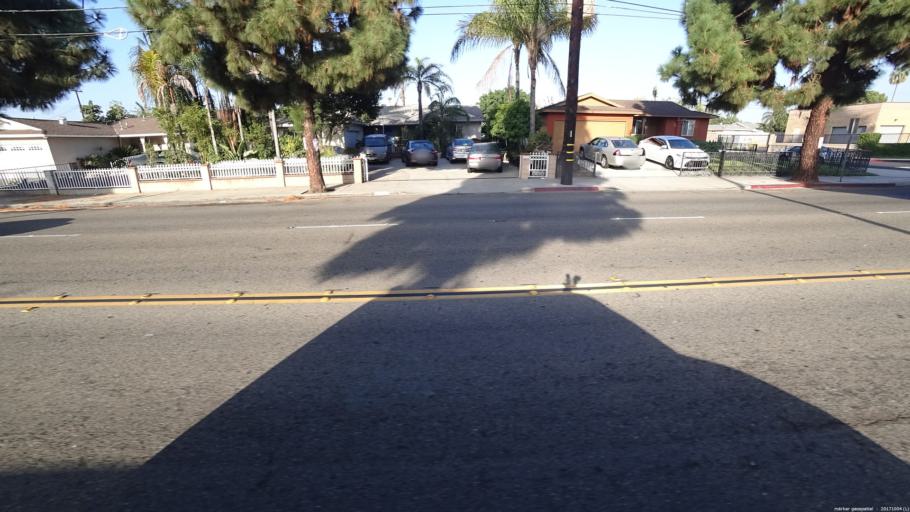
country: US
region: California
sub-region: Orange County
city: Garden Grove
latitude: 33.7870
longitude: -117.9061
